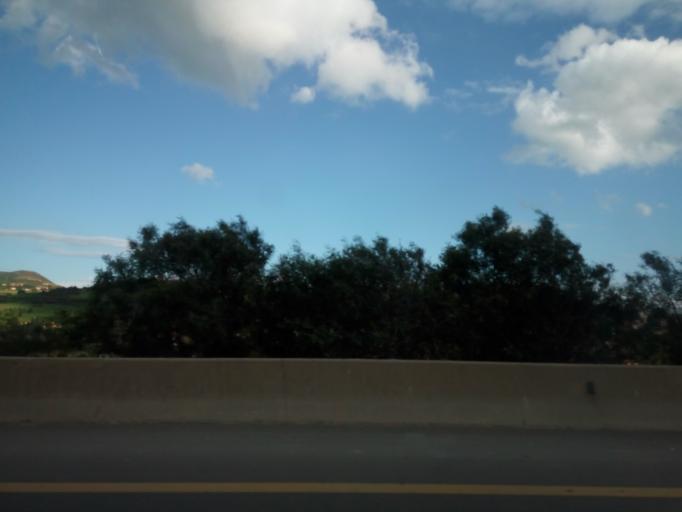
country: DZ
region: Tipaza
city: Hadjout
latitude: 36.3792
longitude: 2.4786
